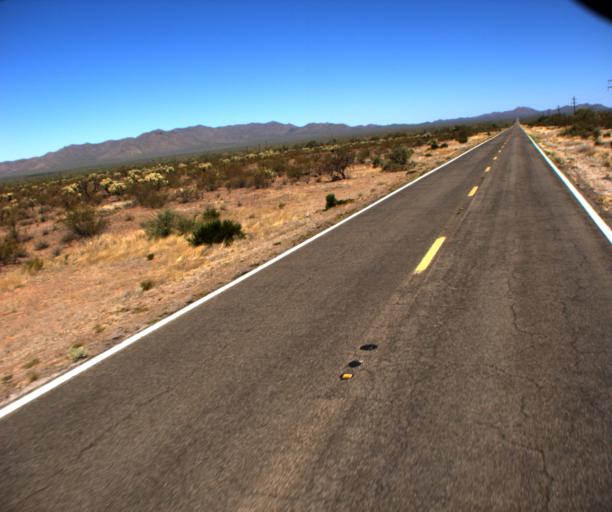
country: US
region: Arizona
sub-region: Pima County
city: Sells
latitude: 32.0724
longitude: -112.0433
